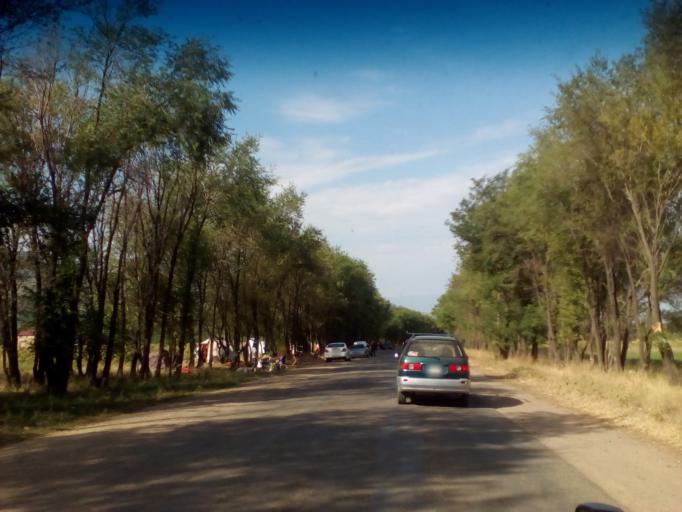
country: KZ
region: Almaty Oblysy
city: Burunday
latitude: 43.1657
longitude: 76.3946
